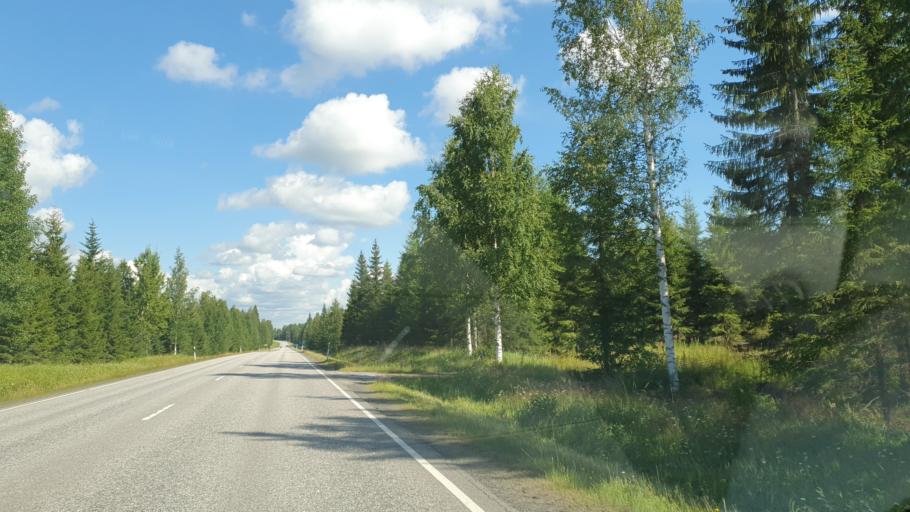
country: FI
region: Northern Savo
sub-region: Ylae-Savo
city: Sonkajaervi
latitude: 63.6891
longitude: 27.3454
